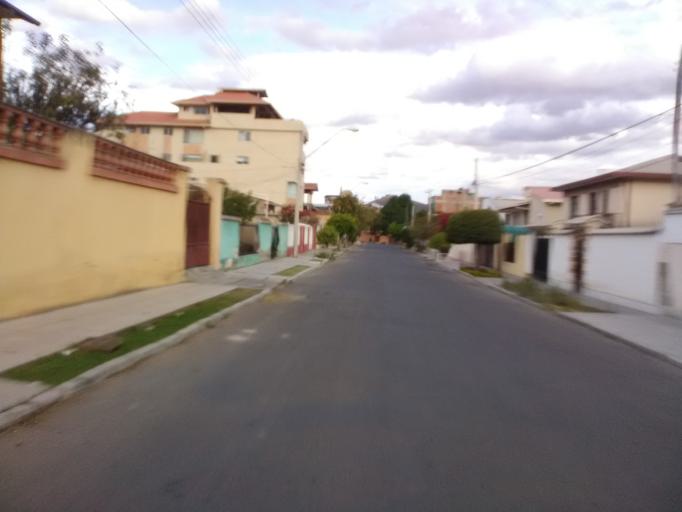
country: BO
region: Cochabamba
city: Cochabamba
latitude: -17.3661
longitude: -66.1626
